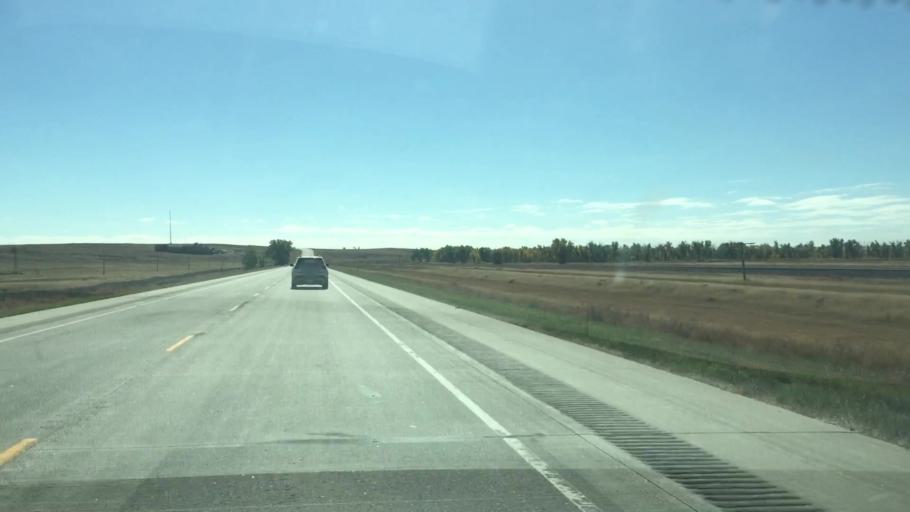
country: US
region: Colorado
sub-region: Lincoln County
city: Limon
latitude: 39.2238
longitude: -103.6100
